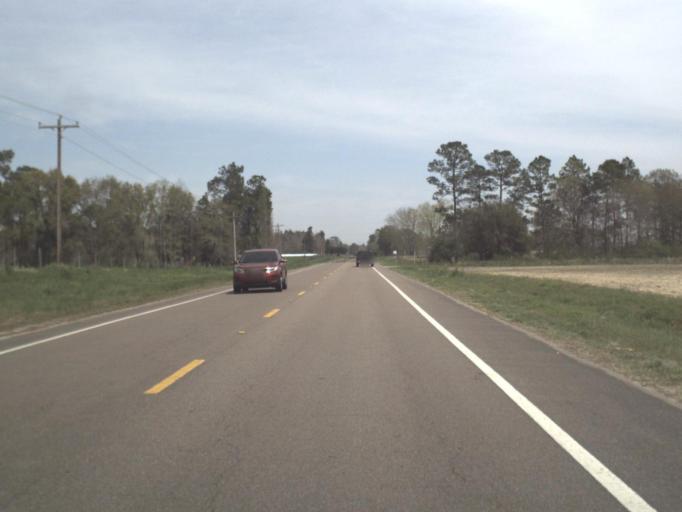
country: US
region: Alabama
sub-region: Geneva County
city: Hartford
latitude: 30.9563
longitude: -85.7167
